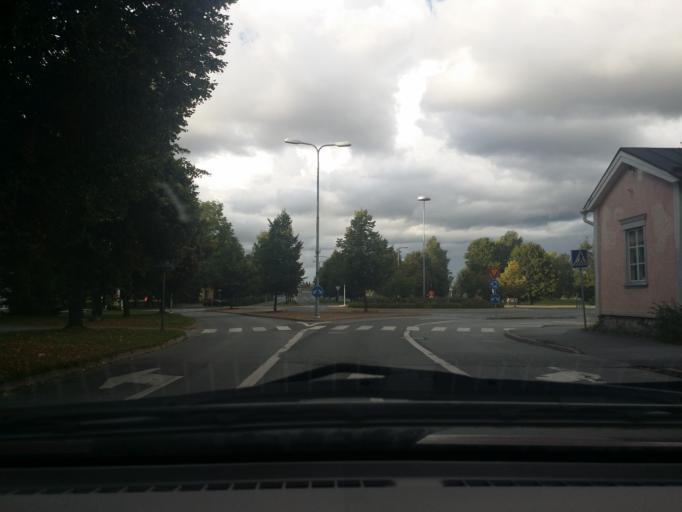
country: FI
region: Satakunta
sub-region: Pori
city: Pori
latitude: 61.4876
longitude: 21.8027
